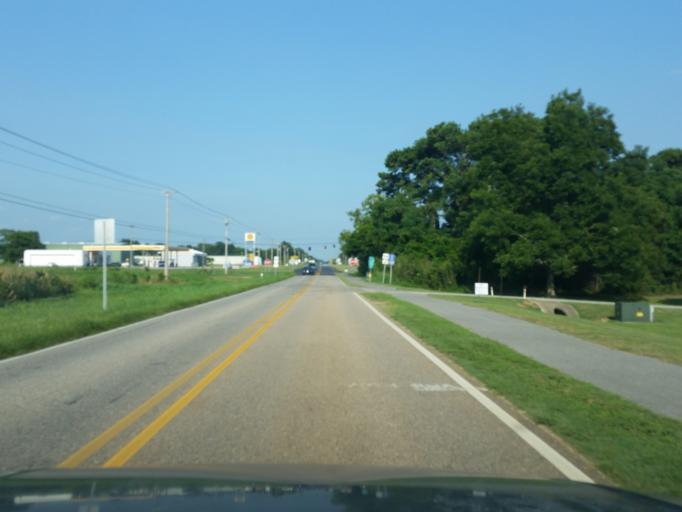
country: US
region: Alabama
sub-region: Baldwin County
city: Point Clear
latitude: 30.4212
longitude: -87.8880
